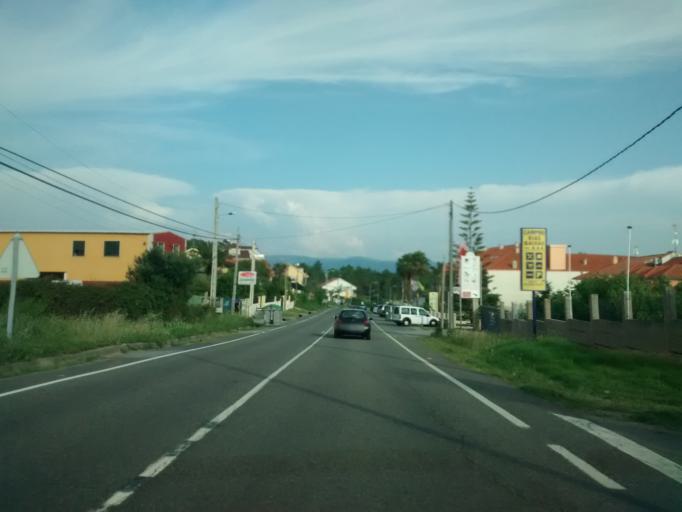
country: ES
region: Galicia
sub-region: Provincia de Pontevedra
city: Sanxenxo
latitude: 42.4037
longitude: -8.8513
